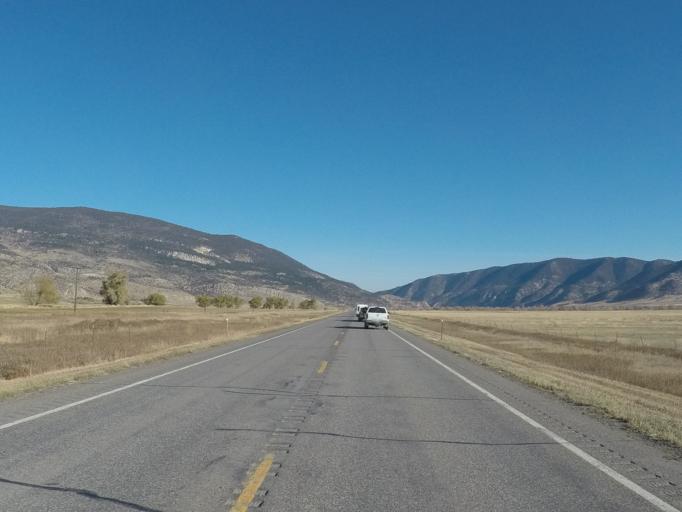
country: US
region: Montana
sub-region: Park County
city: Livingston
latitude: 45.5445
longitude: -110.5997
